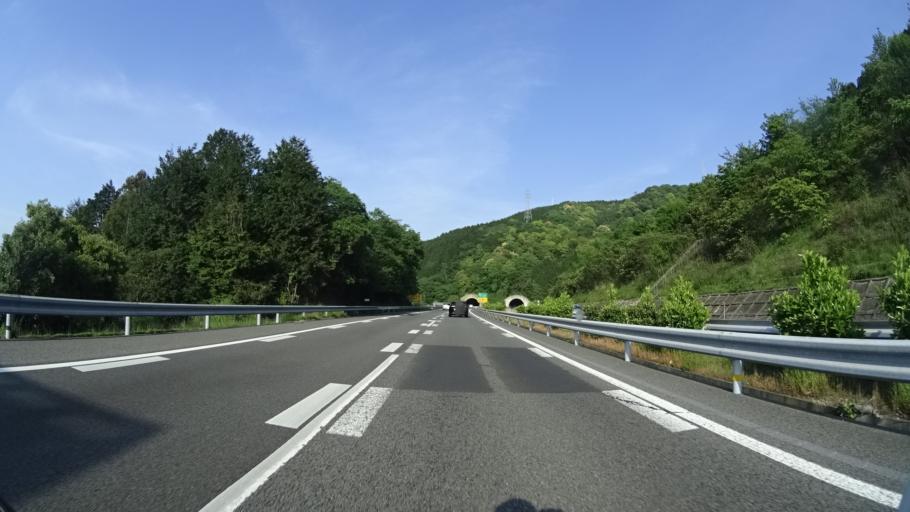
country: JP
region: Ehime
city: Saijo
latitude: 33.9064
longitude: 133.2102
